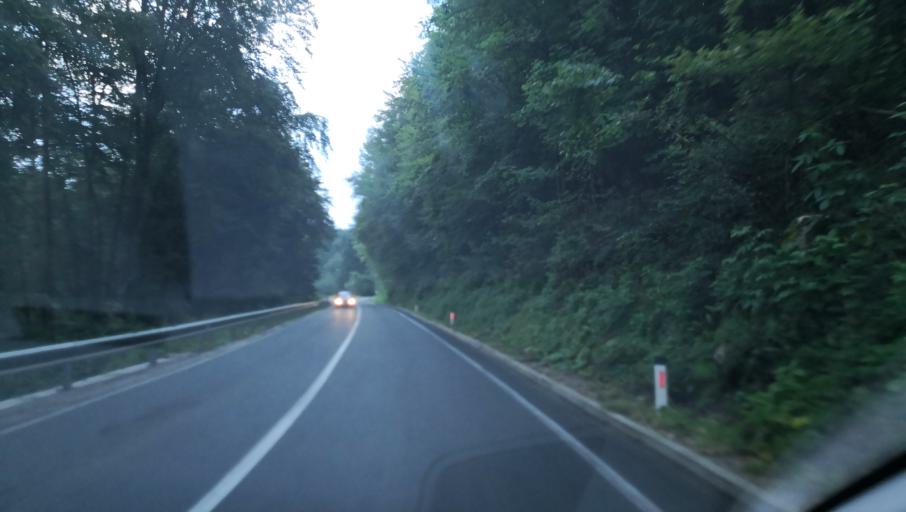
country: SI
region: Novo Mesto
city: Novo Mesto
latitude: 45.7321
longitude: 15.2260
